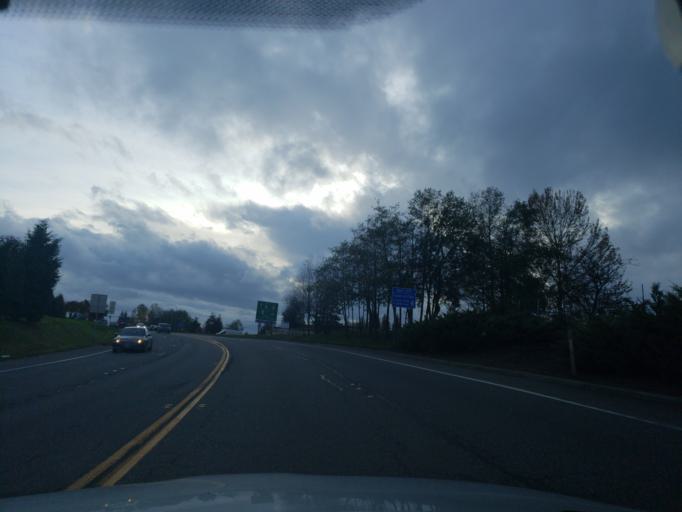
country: US
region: Washington
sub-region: Snohomish County
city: Mukilteo
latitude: 47.9240
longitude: -122.2895
